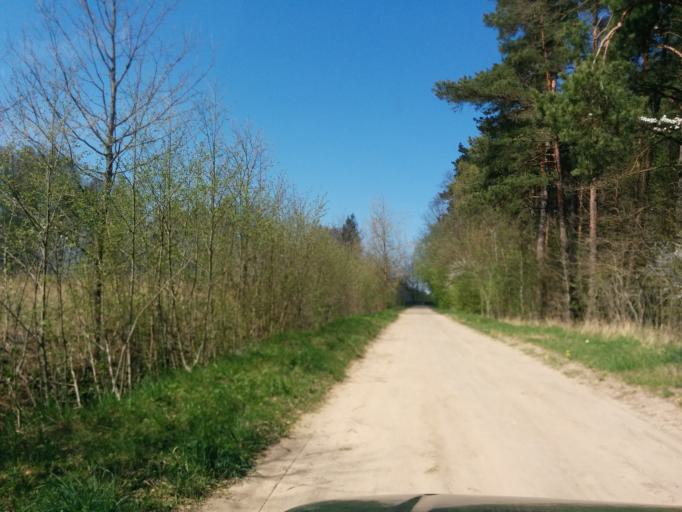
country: LV
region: Jelgava
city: Jelgava
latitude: 56.6202
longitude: 23.7384
